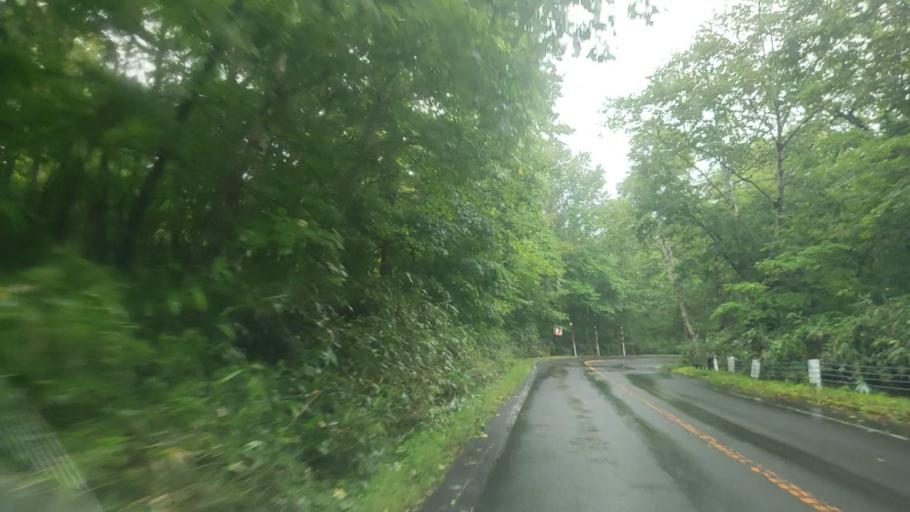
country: JP
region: Hokkaido
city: Shiraoi
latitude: 42.5318
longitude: 141.1124
